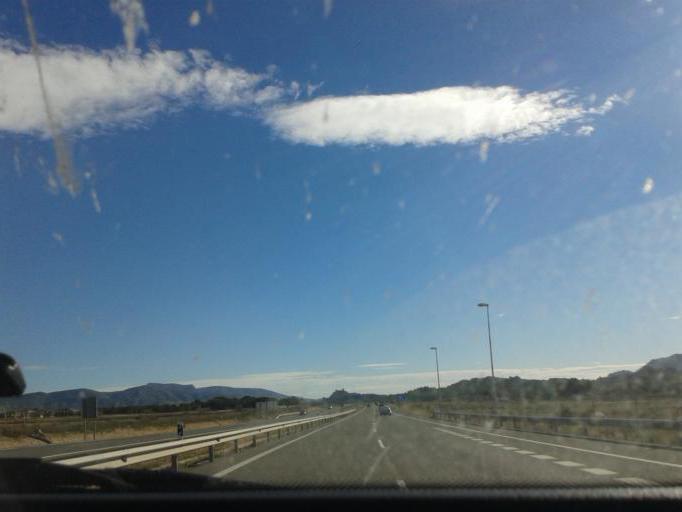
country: ES
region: Valencia
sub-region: Provincia de Alicante
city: Sax
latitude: 38.5700
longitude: -0.8371
